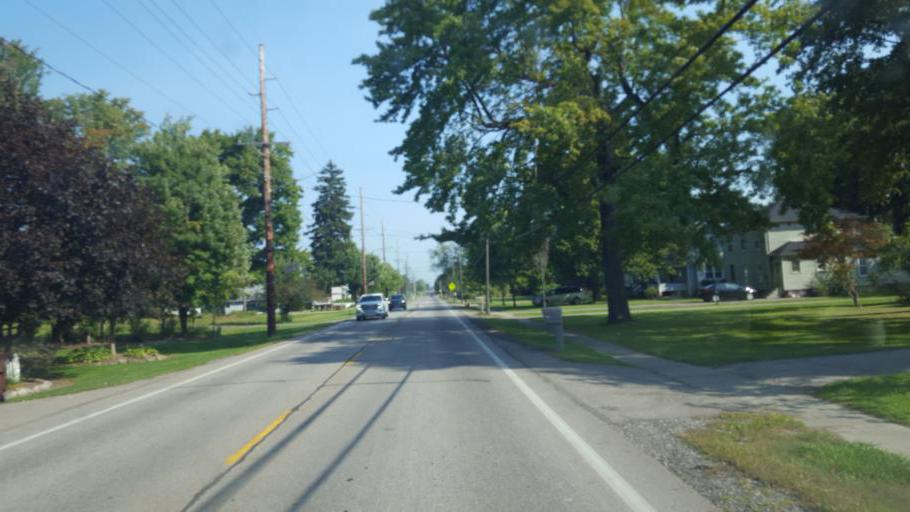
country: US
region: Ohio
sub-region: Ashtabula County
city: Orwell
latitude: 41.5401
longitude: -80.8675
